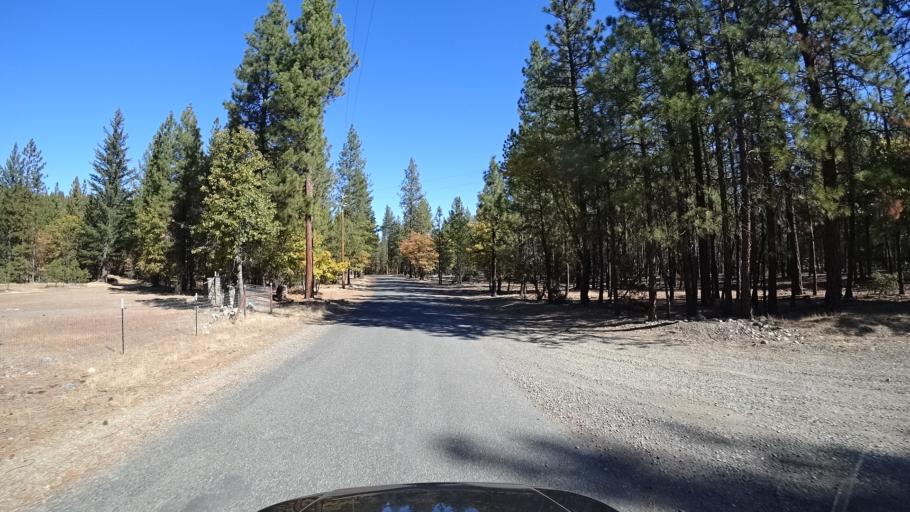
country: US
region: California
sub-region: Siskiyou County
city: Yreka
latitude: 41.5334
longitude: -122.9601
